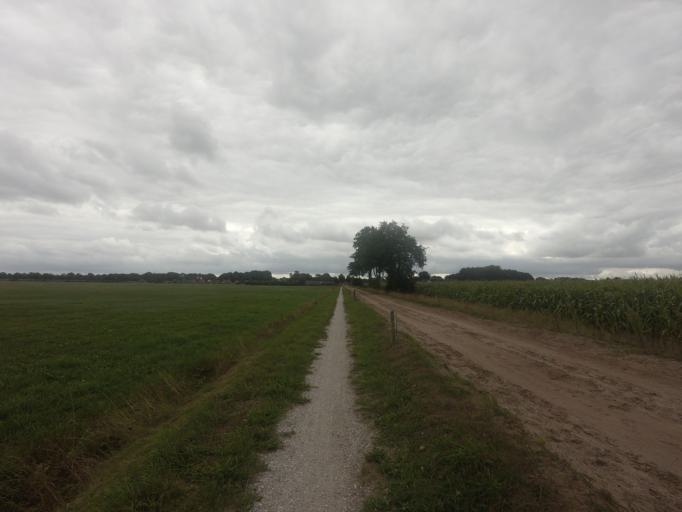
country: NL
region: Friesland
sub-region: Gemeente Weststellingwerf
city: Noordwolde
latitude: 52.9145
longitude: 6.1980
